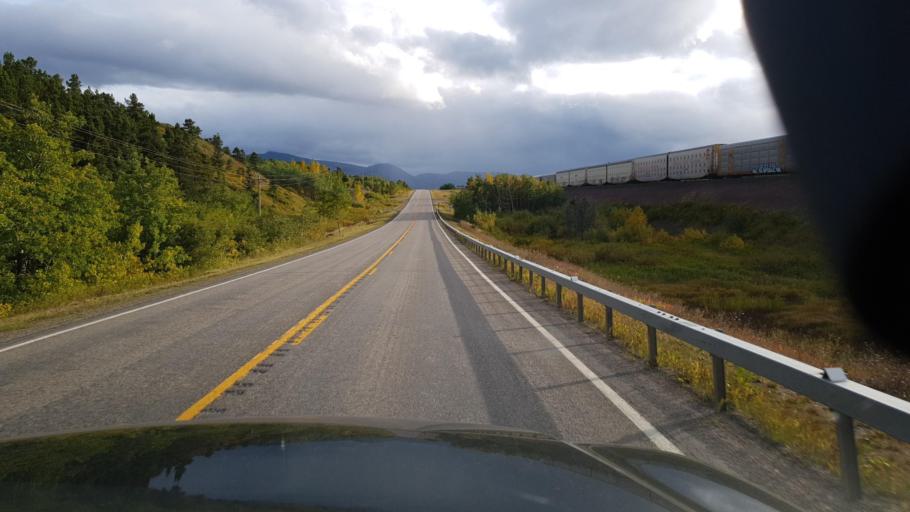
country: US
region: Montana
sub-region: Glacier County
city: South Browning
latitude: 48.3783
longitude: -113.2756
